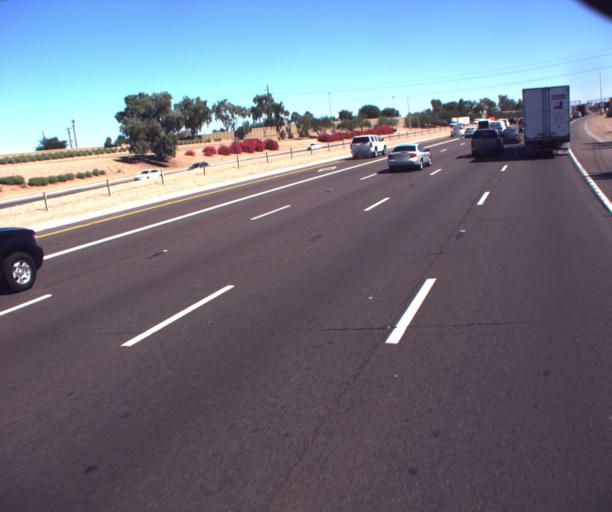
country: US
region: Arizona
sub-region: Maricopa County
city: Phoenix
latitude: 33.4627
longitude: -112.1341
